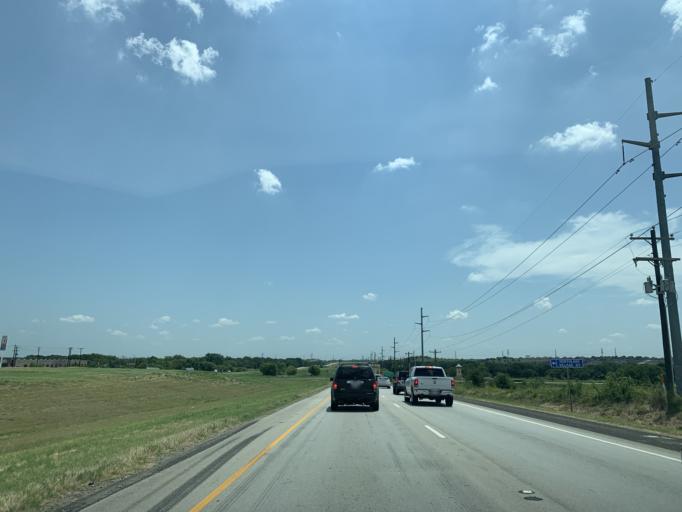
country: US
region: Texas
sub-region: Denton County
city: Roanoke
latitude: 33.0241
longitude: -97.2601
